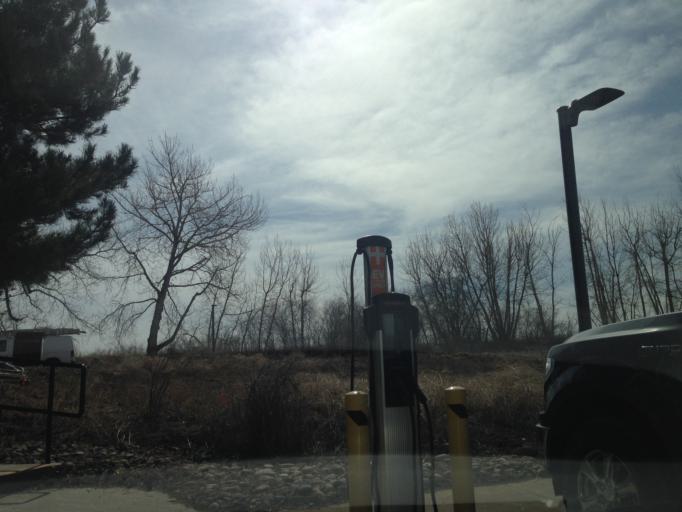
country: US
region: Colorado
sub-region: Boulder County
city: Gunbarrel
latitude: 40.0239
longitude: -105.1830
